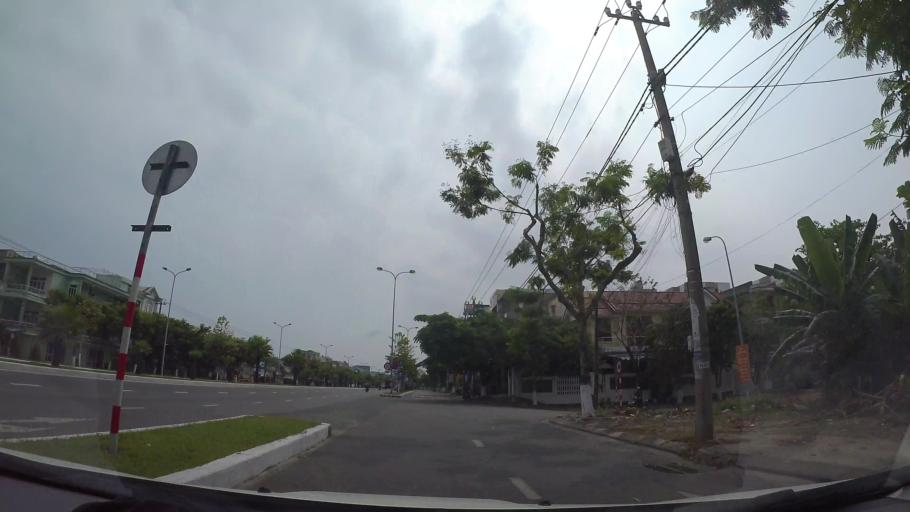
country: VN
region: Da Nang
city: Da Nang
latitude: 16.0901
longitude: 108.2423
